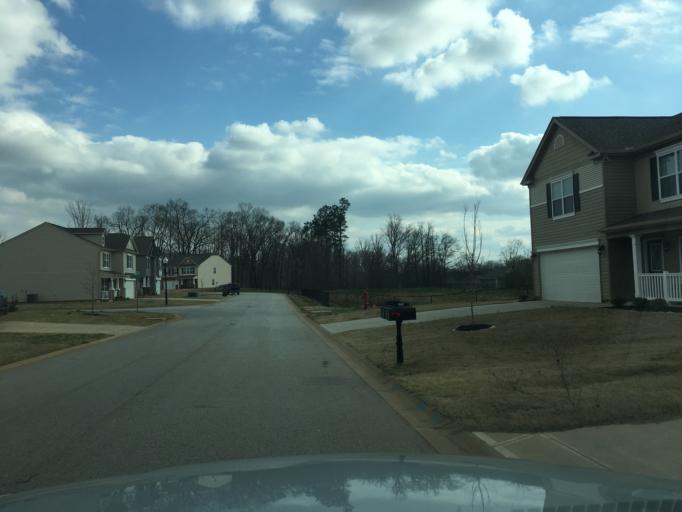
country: US
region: South Carolina
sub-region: Spartanburg County
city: Duncan
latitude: 34.8924
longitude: -82.1259
